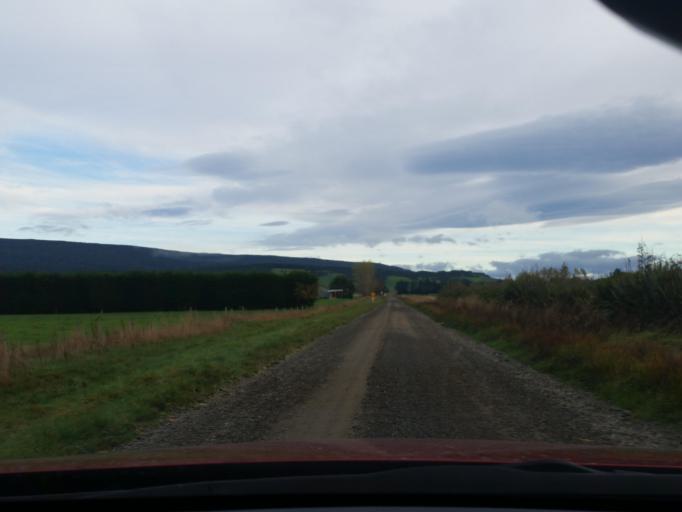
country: NZ
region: Southland
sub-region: Southland District
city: Riverton
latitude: -46.0997
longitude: 167.9670
